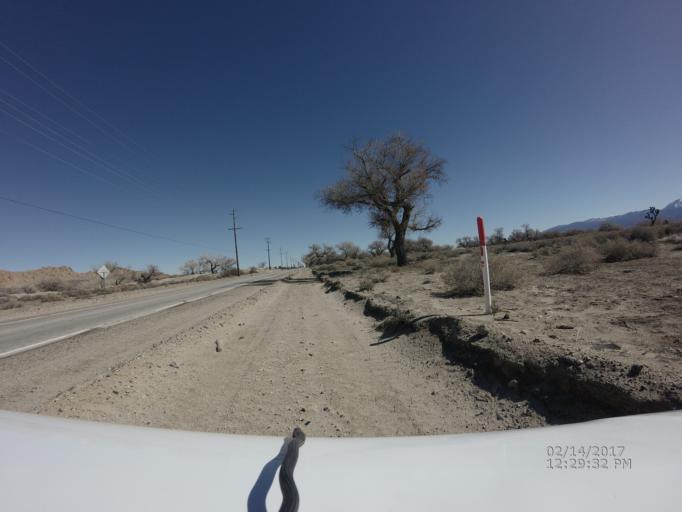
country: US
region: California
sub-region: Los Angeles County
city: Lake Los Angeles
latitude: 34.5800
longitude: -117.8734
